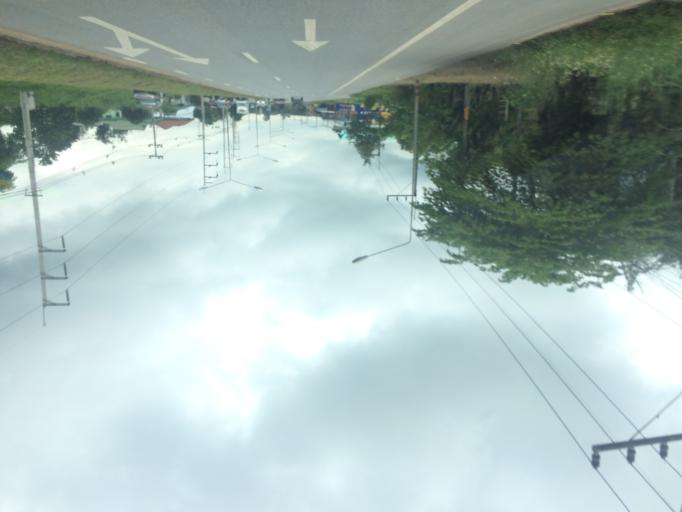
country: TH
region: Chiang Rai
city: Mae Chan
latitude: 20.0836
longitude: 99.8747
